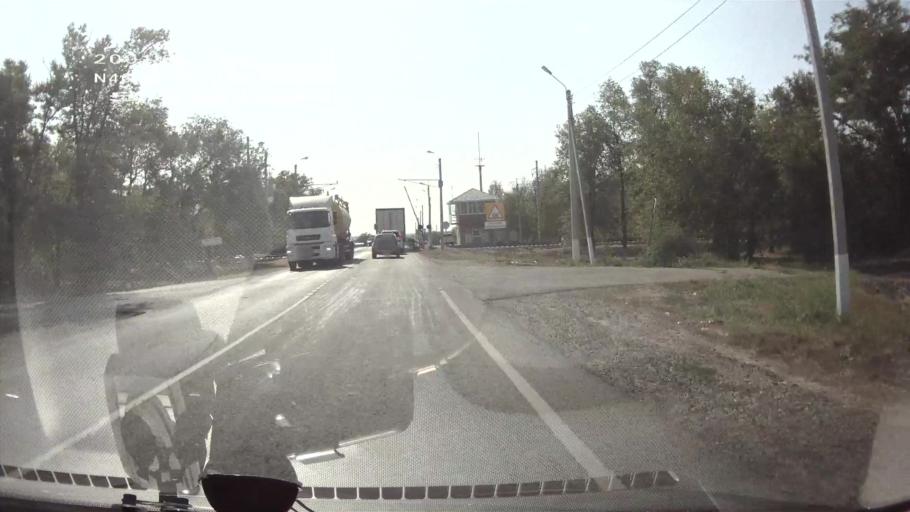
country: RU
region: Krasnodarskiy
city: Belaya Glina
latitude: 46.0994
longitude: 40.8538
